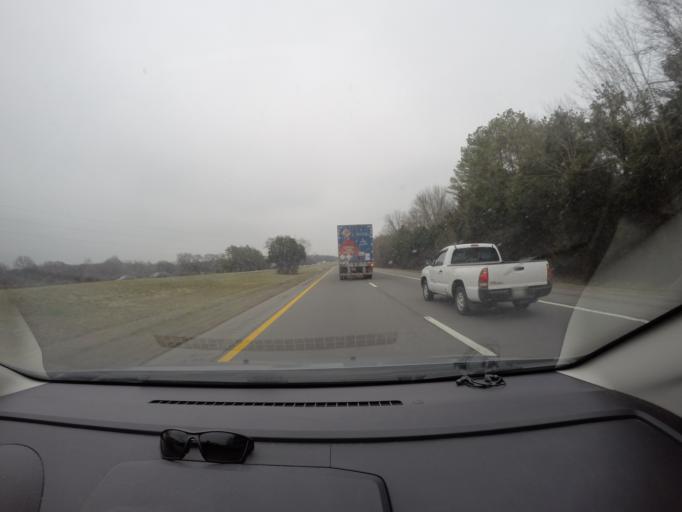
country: US
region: Tennessee
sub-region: Rutherford County
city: Plainview
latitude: 35.7537
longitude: -86.3463
